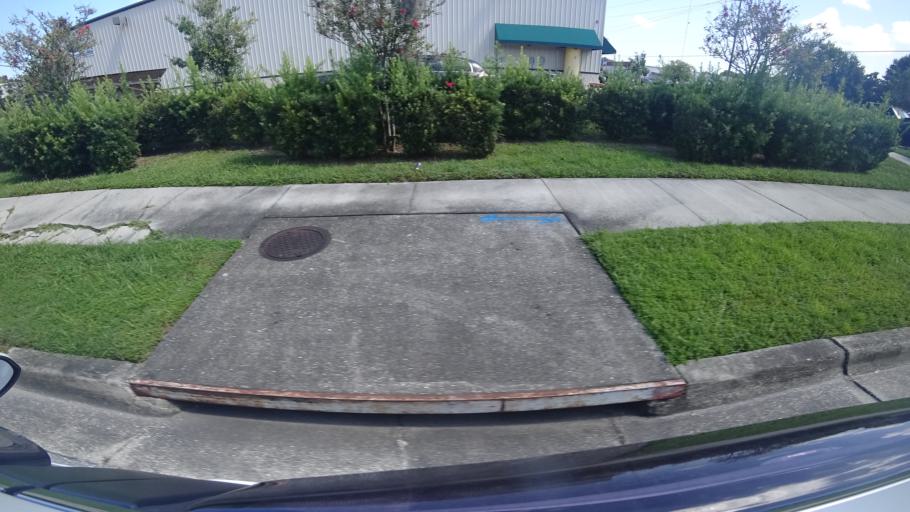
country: US
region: Florida
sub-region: Manatee County
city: Whitfield
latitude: 27.4219
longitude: -82.5408
